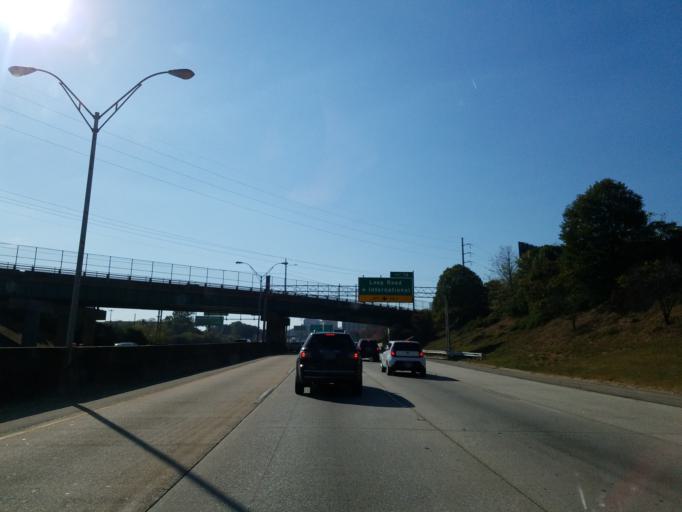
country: US
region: Georgia
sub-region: Fulton County
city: Hapeville
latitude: 33.6643
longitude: -84.4211
